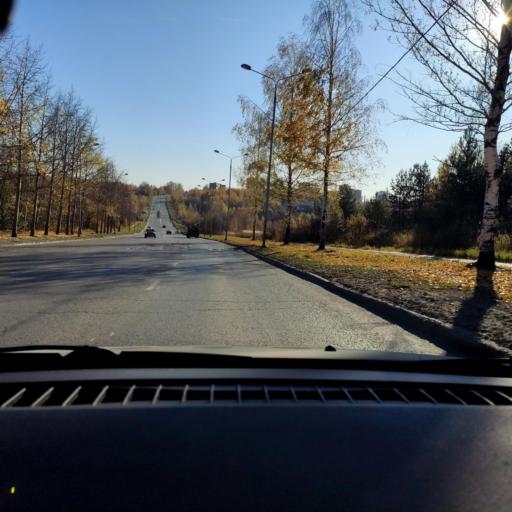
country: RU
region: Perm
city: Perm
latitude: 58.0739
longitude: 56.3681
